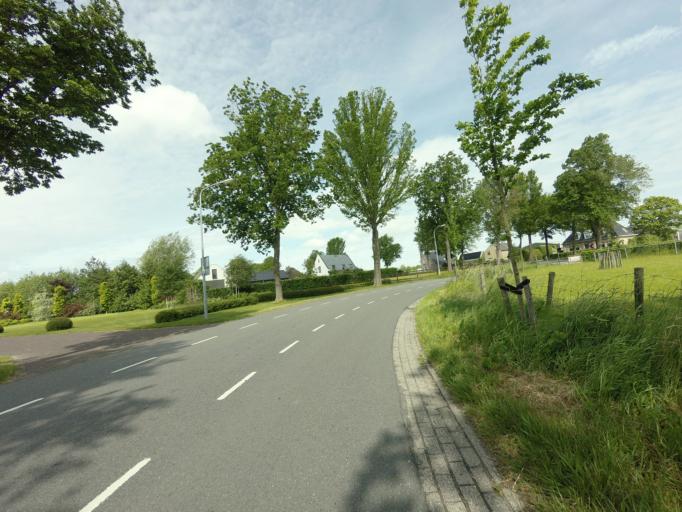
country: NL
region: North Holland
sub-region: Gemeente Hoorn
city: Hoorn
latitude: 52.6921
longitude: 5.0404
